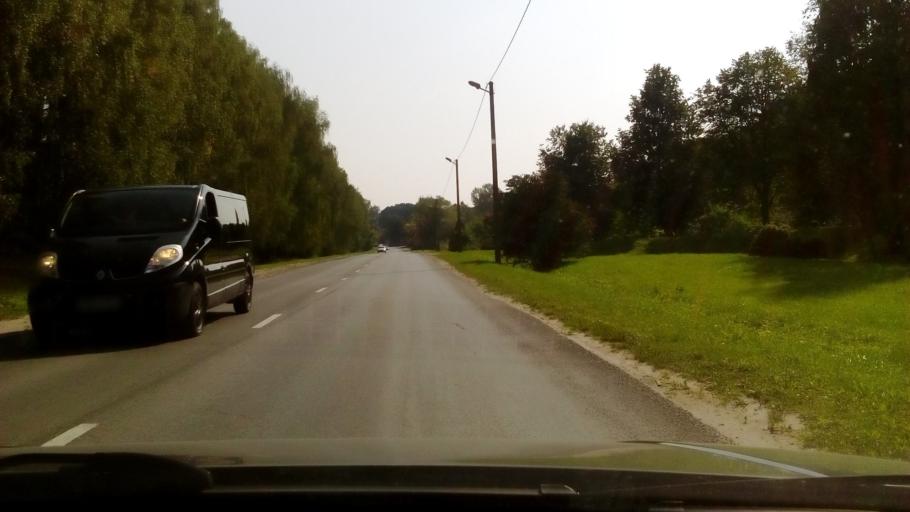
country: LT
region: Alytaus apskritis
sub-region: Alytus
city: Alytus
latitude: 54.4059
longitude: 24.0339
